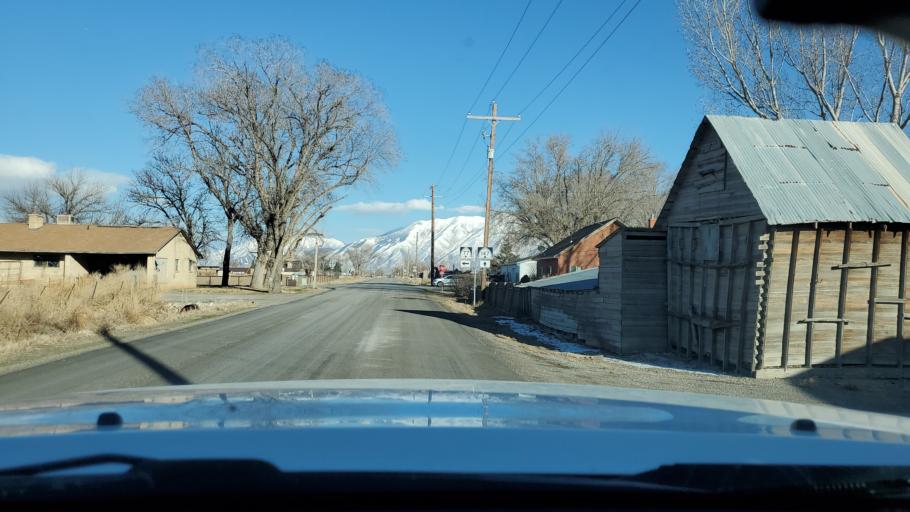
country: US
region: Utah
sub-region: Utah County
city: Benjamin
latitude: 40.1146
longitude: -111.7315
